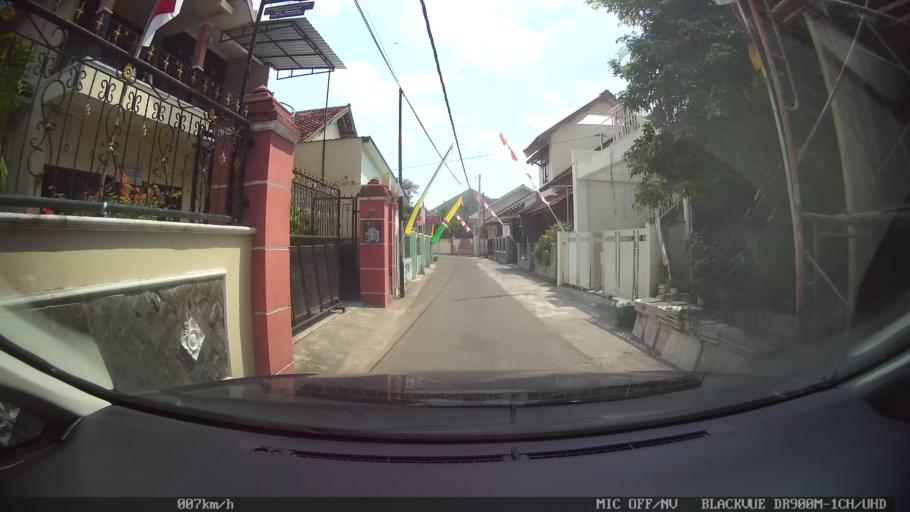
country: ID
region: Daerah Istimewa Yogyakarta
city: Depok
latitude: -7.8044
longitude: 110.4074
